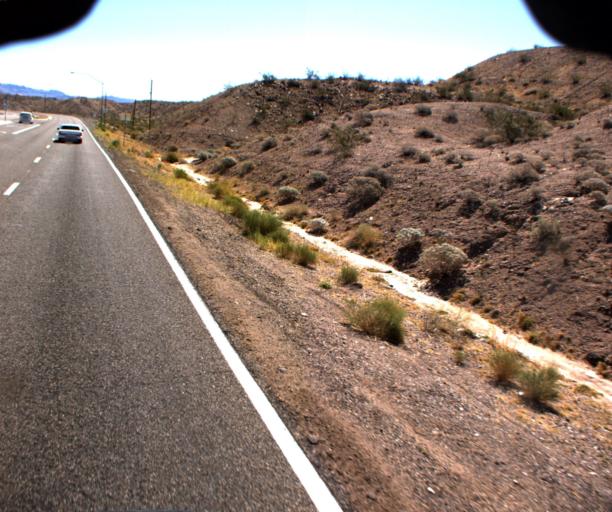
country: US
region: Nevada
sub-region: Clark County
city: Laughlin
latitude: 35.1864
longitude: -114.5528
